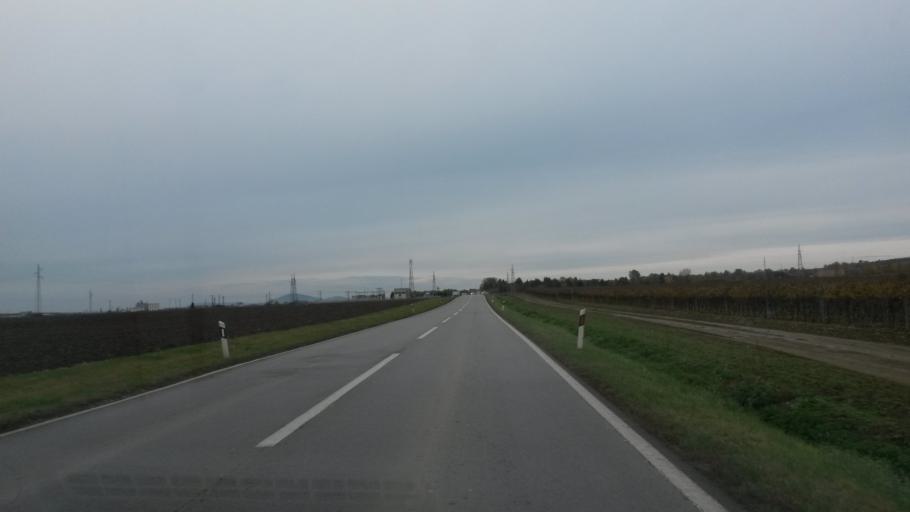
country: HR
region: Osjecko-Baranjska
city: Beli Manastir
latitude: 45.7550
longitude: 18.6343
